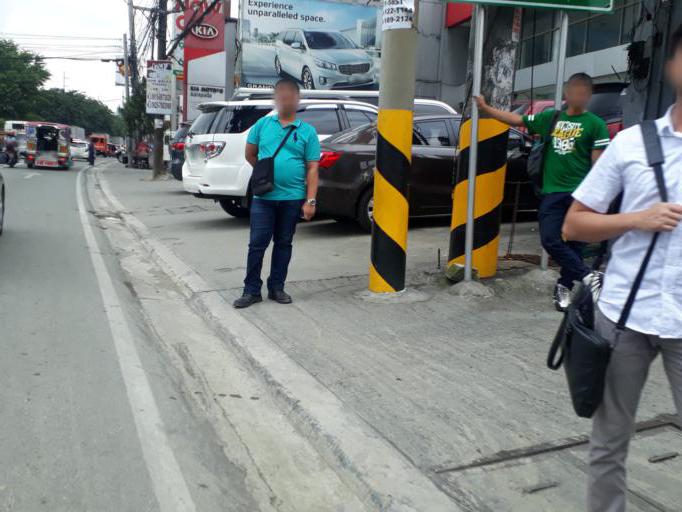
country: PH
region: Metro Manila
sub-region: Marikina
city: Calumpang
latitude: 14.6061
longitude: 121.0789
